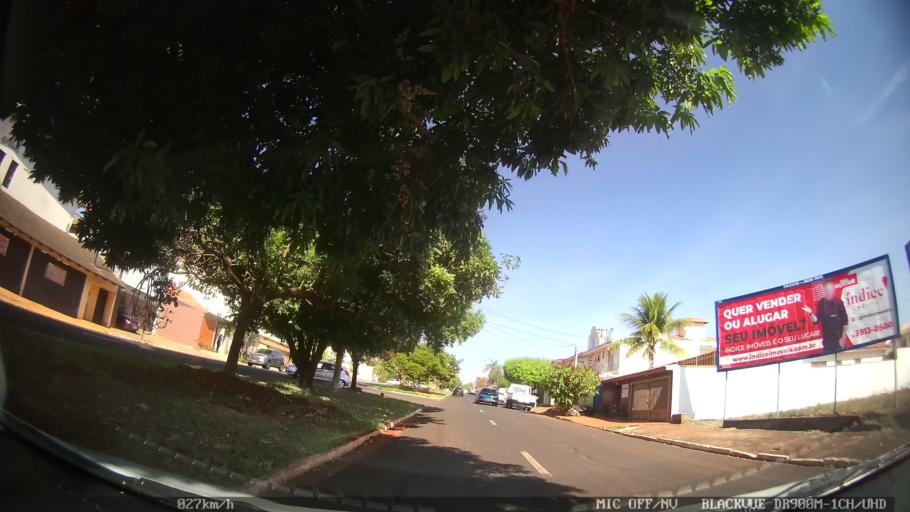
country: BR
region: Sao Paulo
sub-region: Ribeirao Preto
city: Ribeirao Preto
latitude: -21.2074
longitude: -47.8162
